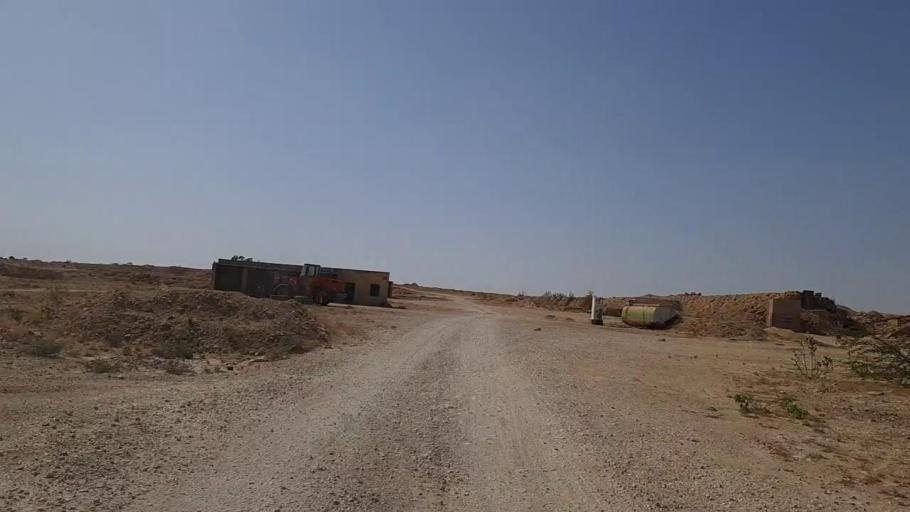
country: PK
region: Sindh
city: Kotri
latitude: 25.1649
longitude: 68.1968
